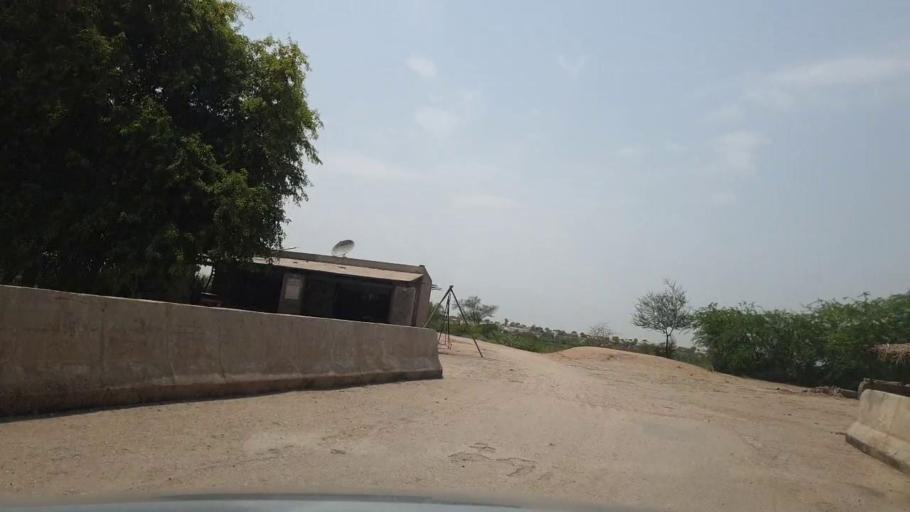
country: PK
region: Sindh
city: Pano Aqil
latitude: 27.5904
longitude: 69.2028
